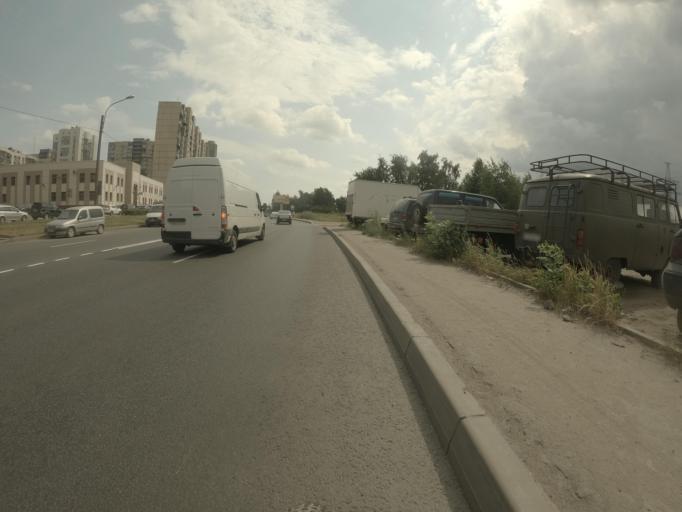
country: RU
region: St.-Petersburg
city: Krasnogvargeisky
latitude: 59.9375
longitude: 30.4708
